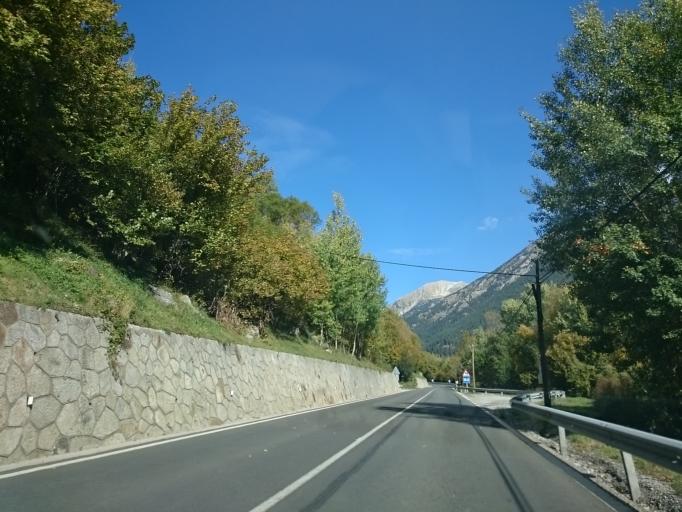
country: ES
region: Aragon
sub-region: Provincia de Huesca
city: Bonansa
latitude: 42.5513
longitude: 0.7470
